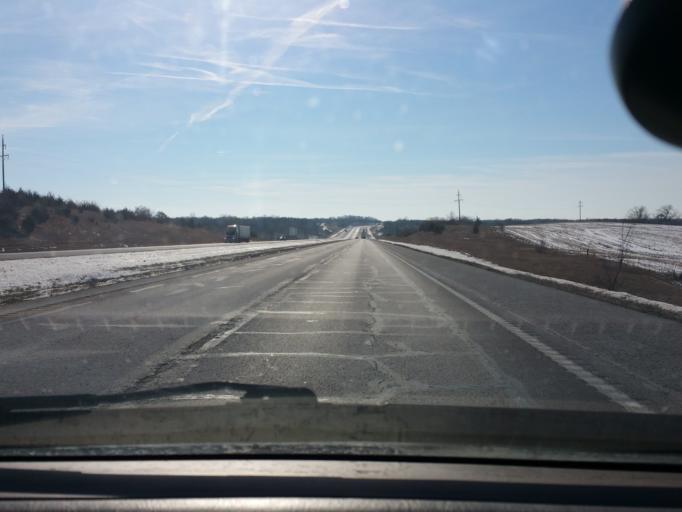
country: US
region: Missouri
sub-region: Harrison County
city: Bethany
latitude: 40.1968
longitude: -94.0143
